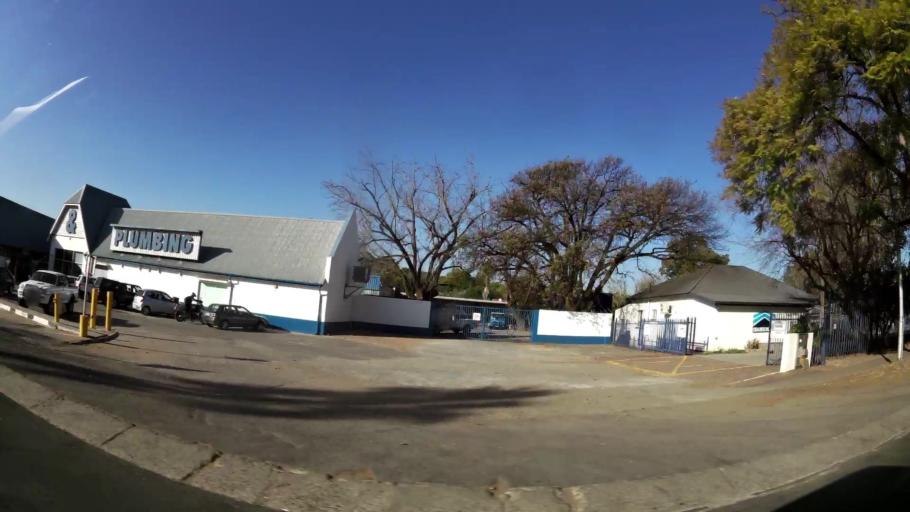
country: ZA
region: Gauteng
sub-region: City of Tshwane Metropolitan Municipality
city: Pretoria
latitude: -25.7287
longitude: 28.2153
